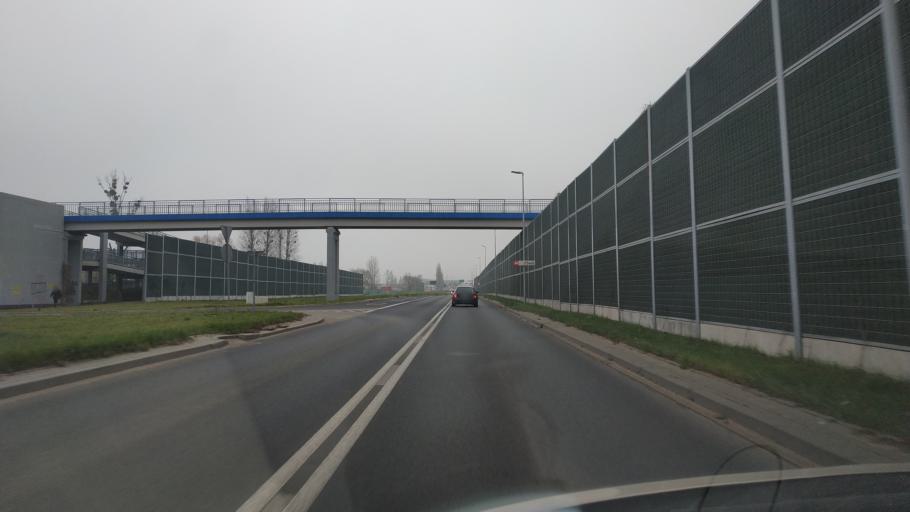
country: PL
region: Kujawsko-Pomorskie
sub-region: Torun
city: Torun
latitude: 53.0285
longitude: 18.6164
